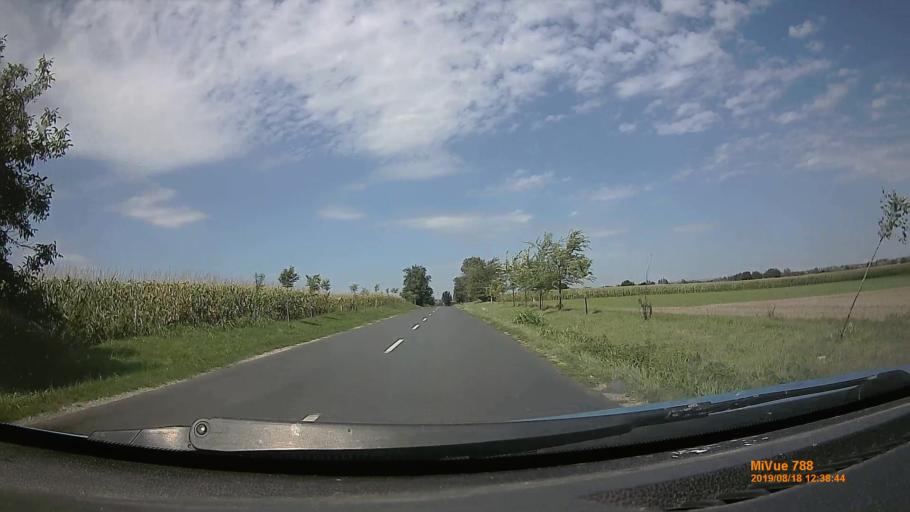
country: HU
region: Fejer
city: Szabadbattyan
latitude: 47.0913
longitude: 18.3961
